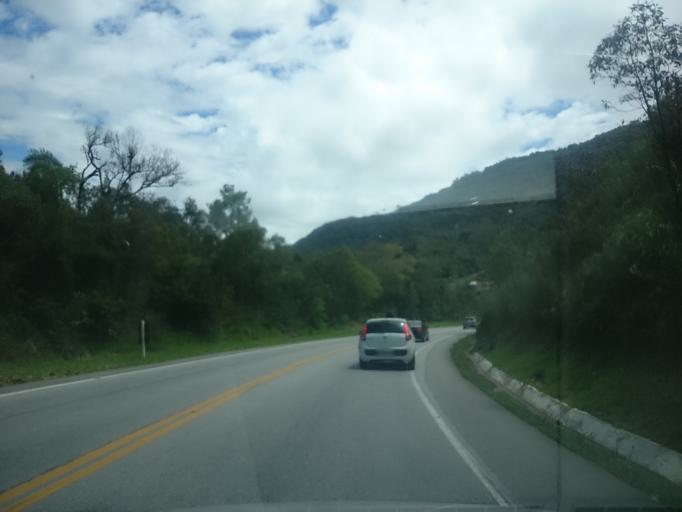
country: BR
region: Santa Catarina
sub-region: Anitapolis
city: Anitapolis
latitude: -27.6778
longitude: -49.2154
